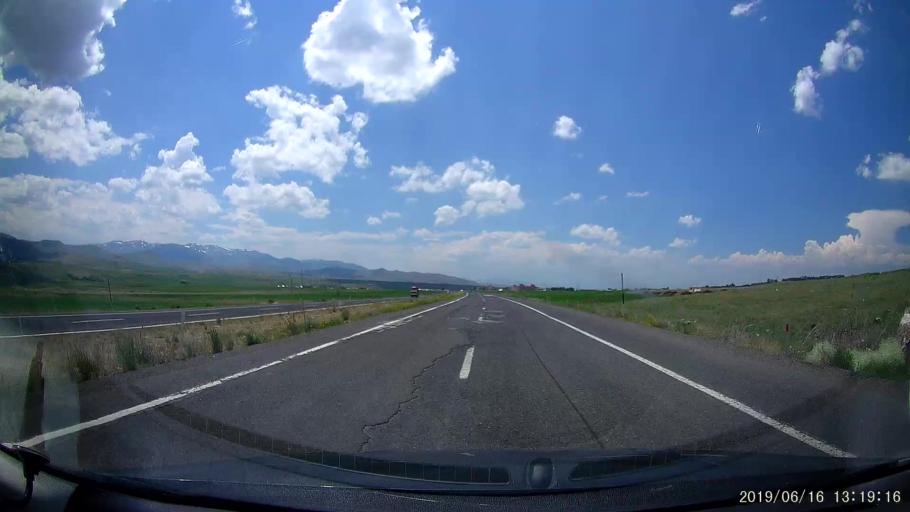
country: TR
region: Agri
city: Taslicay
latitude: 39.6331
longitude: 43.4113
